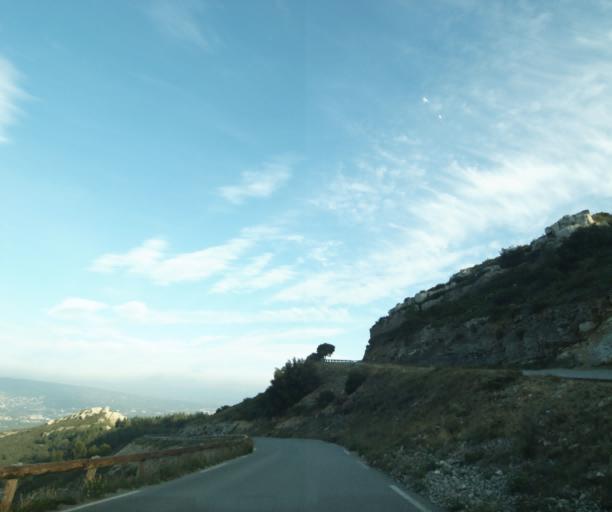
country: FR
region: Provence-Alpes-Cote d'Azur
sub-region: Departement des Bouches-du-Rhone
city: Cassis
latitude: 43.1843
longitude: 5.5640
